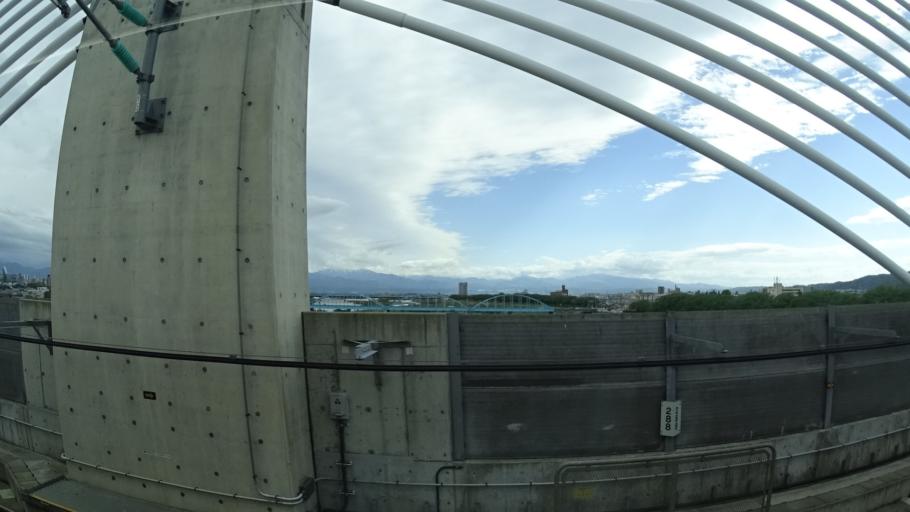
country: JP
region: Toyama
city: Toyama-shi
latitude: 36.7057
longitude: 137.2027
